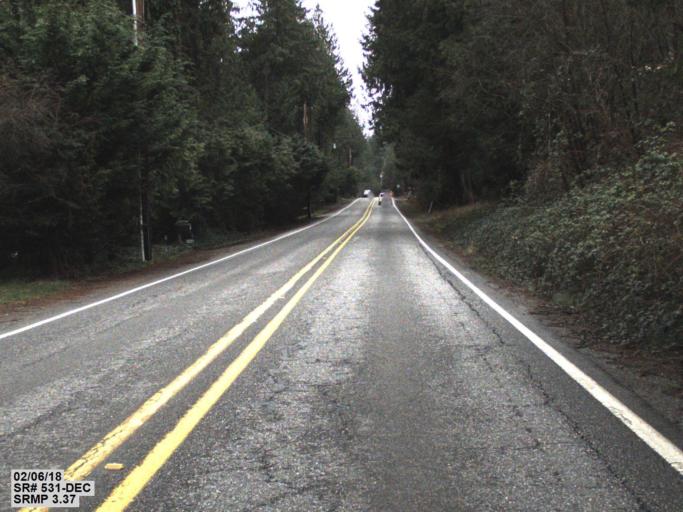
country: US
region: Washington
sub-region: Snohomish County
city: Smokey Point
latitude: 48.1566
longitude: -122.2500
